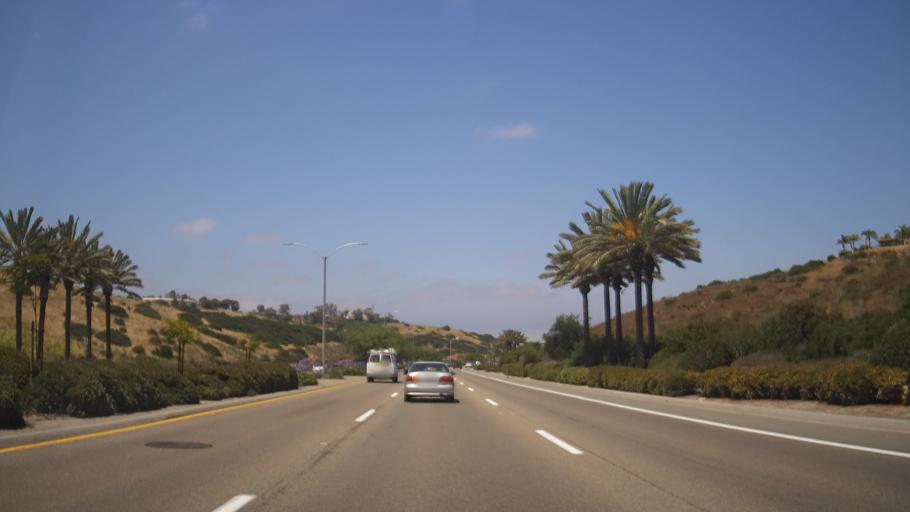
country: US
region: California
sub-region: San Diego County
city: Bonita
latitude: 32.6100
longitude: -117.0161
